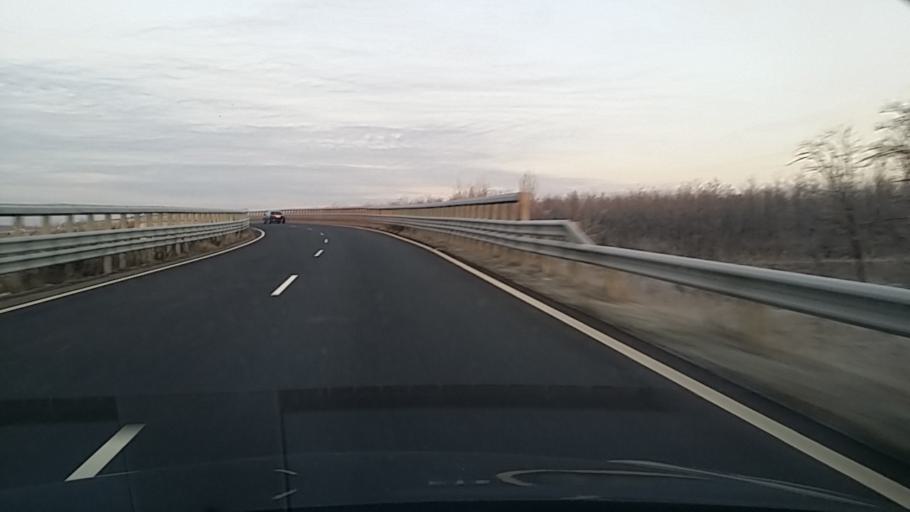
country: HU
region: Pest
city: Dunaharaszti
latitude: 47.3693
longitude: 19.1237
